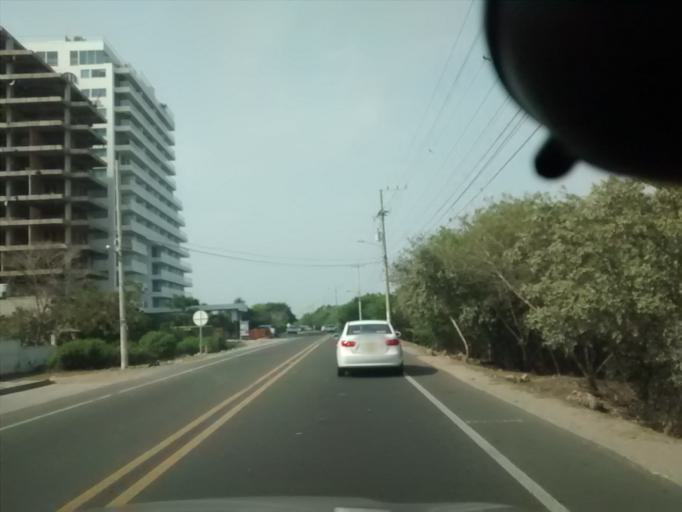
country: CO
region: Bolivar
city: Cartagena
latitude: 10.4665
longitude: -75.4997
